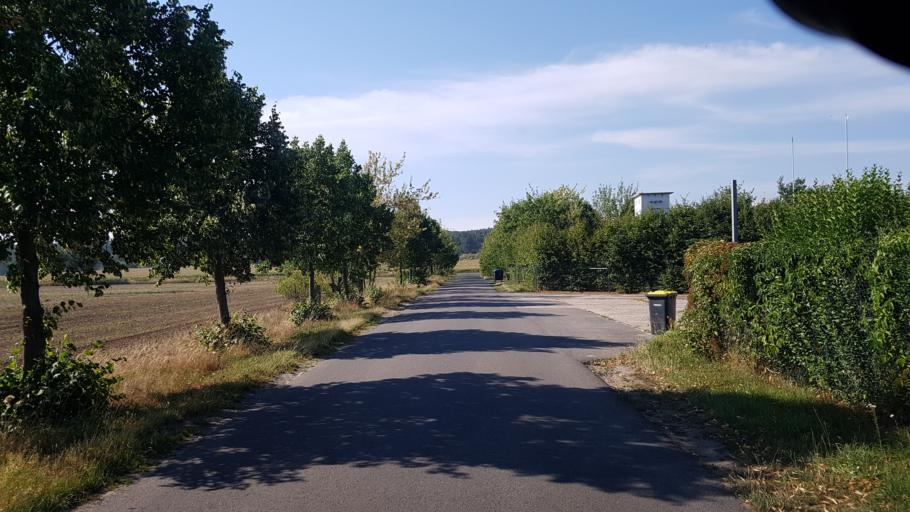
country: DE
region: Brandenburg
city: Groden
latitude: 51.4018
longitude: 13.5879
